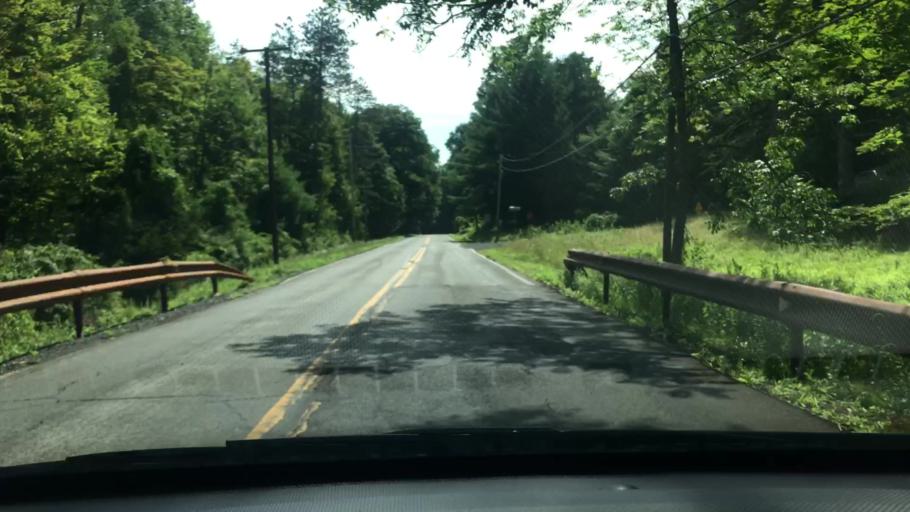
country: US
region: New York
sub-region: Ulster County
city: Shokan
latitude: 41.9503
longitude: -74.2570
